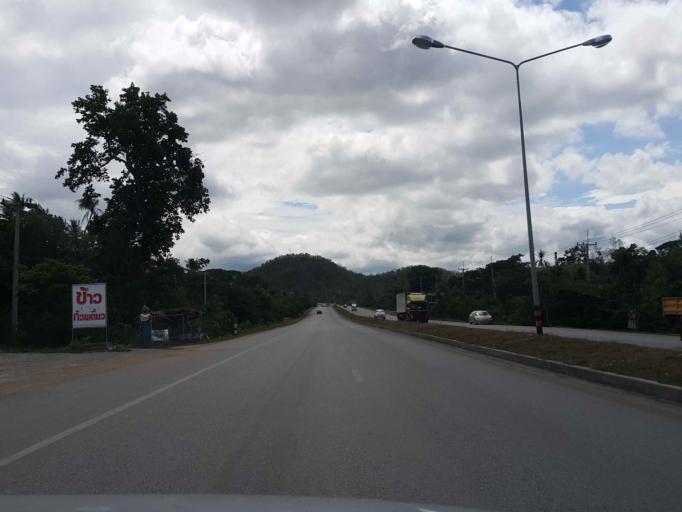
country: TH
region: Tak
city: Tak
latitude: 16.8208
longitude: 99.0765
